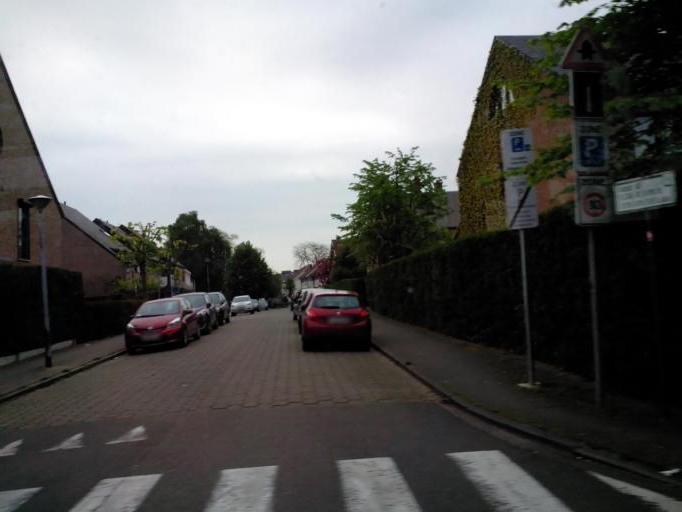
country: BE
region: Flanders
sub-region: Provincie Vlaams-Brabant
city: Diegem
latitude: 50.8589
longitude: 4.4067
